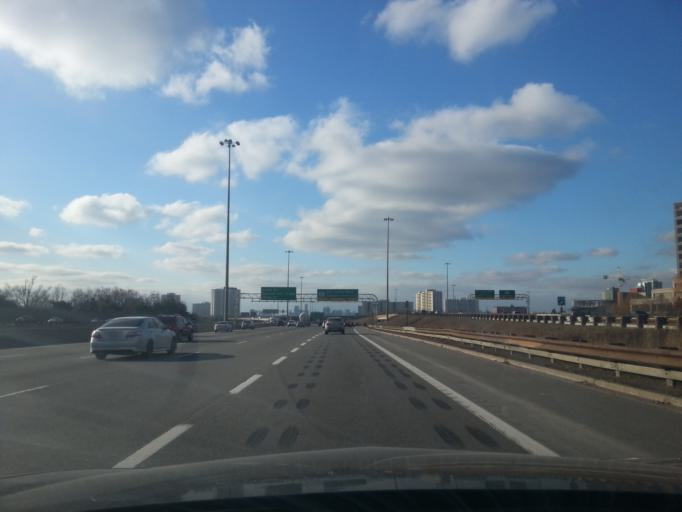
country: CA
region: Ontario
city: Willowdale
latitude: 43.7683
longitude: -79.3287
